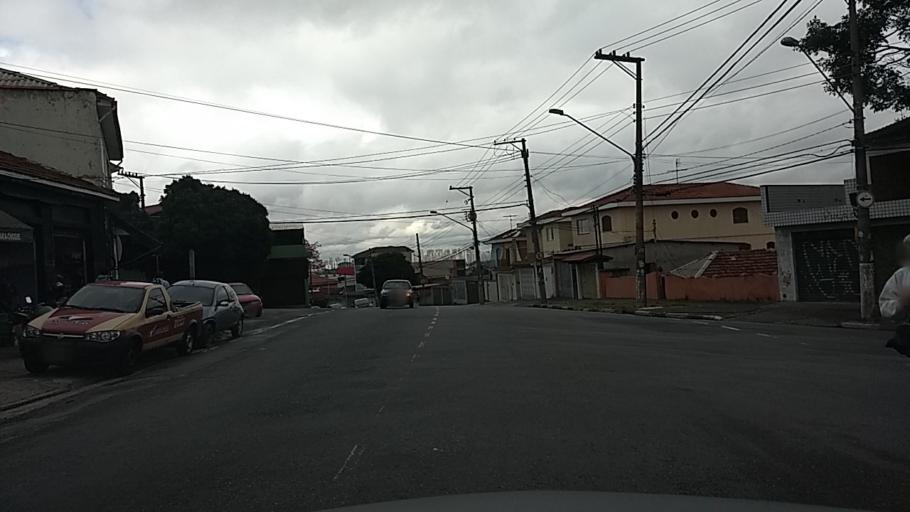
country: BR
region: Sao Paulo
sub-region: Sao Paulo
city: Sao Paulo
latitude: -23.5075
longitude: -46.5948
